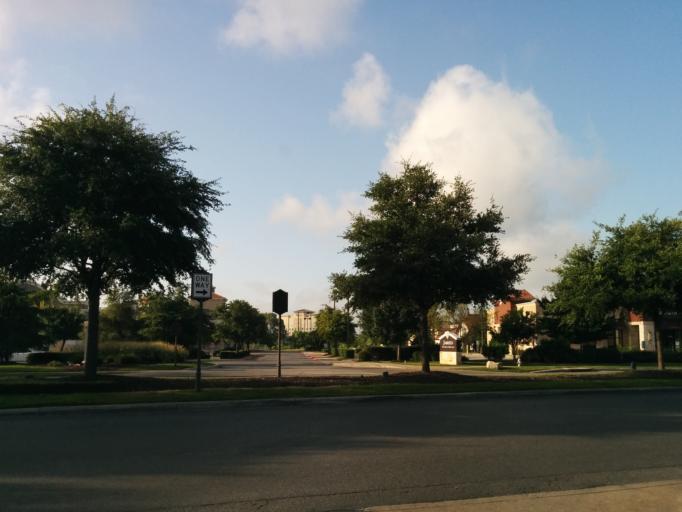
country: US
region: Texas
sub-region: Bexar County
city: Shavano Park
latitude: 29.6066
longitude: -98.6001
